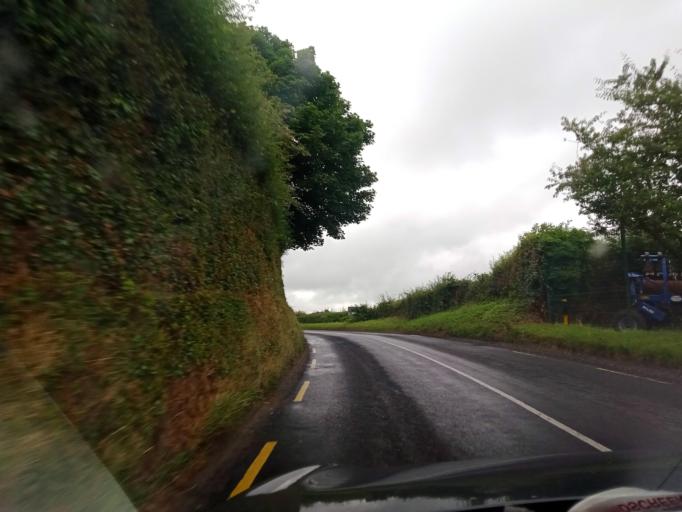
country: IE
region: Leinster
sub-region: Laois
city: Abbeyleix
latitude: 52.9102
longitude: -7.3246
